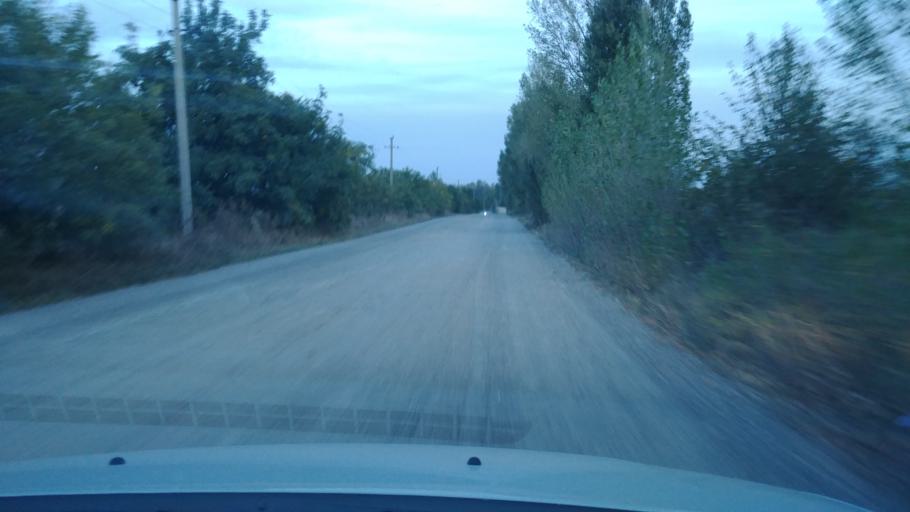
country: MD
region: Rezina
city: Saharna
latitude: 47.6791
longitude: 28.9202
